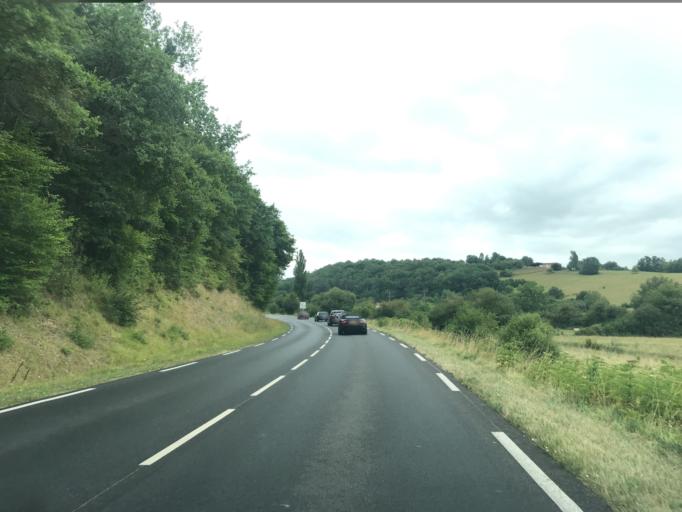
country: FR
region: Aquitaine
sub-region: Departement de la Dordogne
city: Bassillac
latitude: 45.1133
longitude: 0.8326
